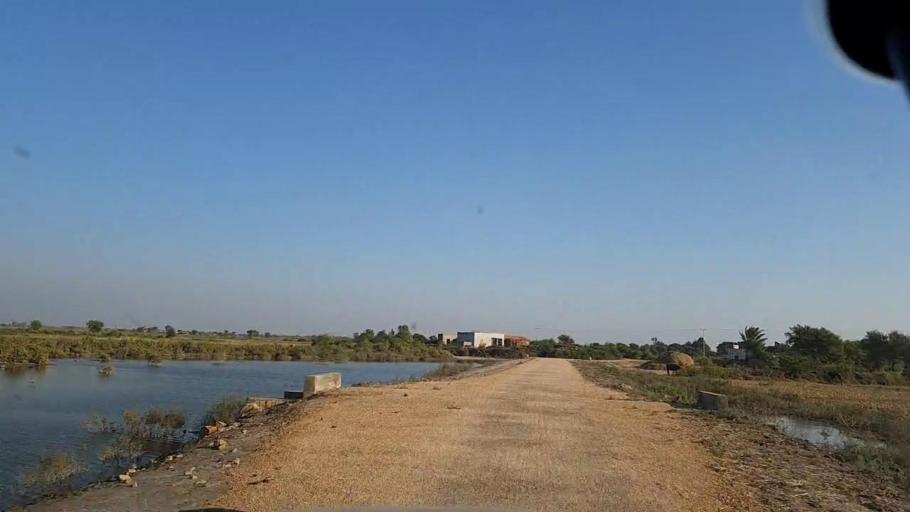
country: PK
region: Sindh
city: Chuhar Jamali
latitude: 24.5618
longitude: 68.0744
